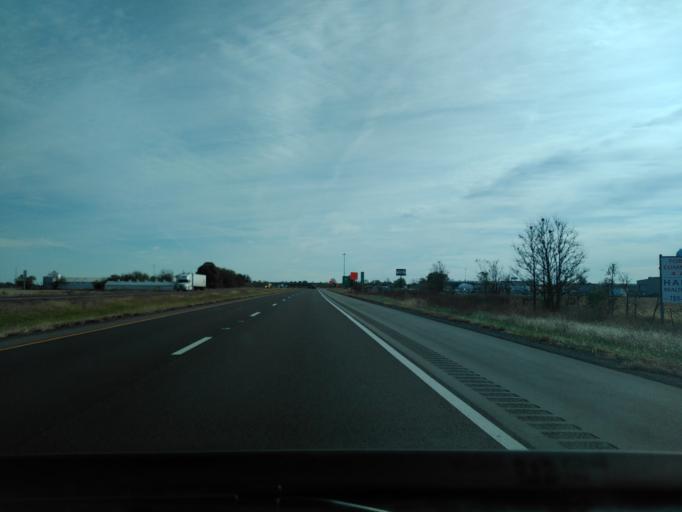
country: US
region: Illinois
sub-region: Madison County
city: Highland
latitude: 38.7863
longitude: -89.6398
